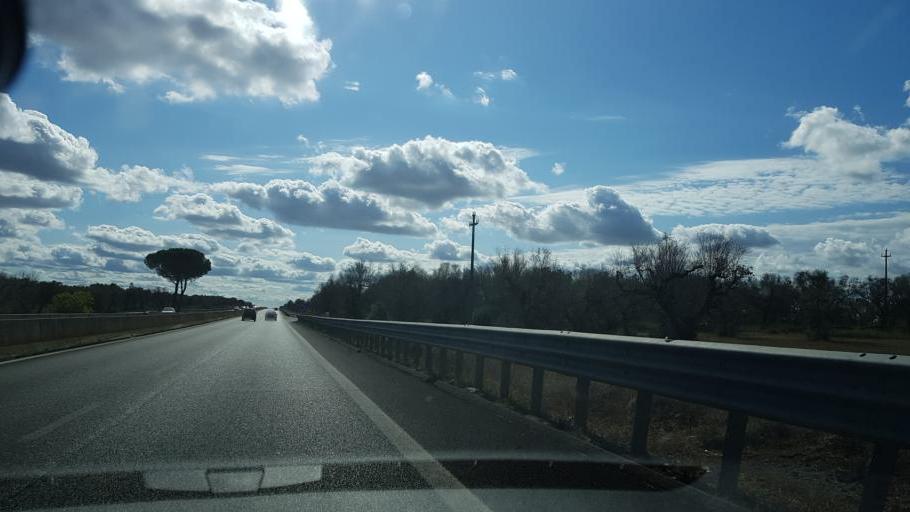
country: IT
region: Apulia
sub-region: Provincia di Lecce
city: Squinzano
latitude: 40.4522
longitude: 18.0662
